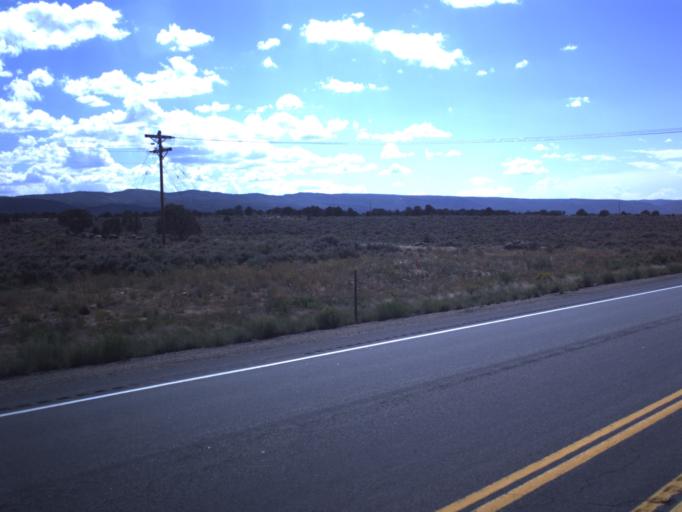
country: US
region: Utah
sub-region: Duchesne County
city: Duchesne
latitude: 40.2065
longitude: -110.7327
